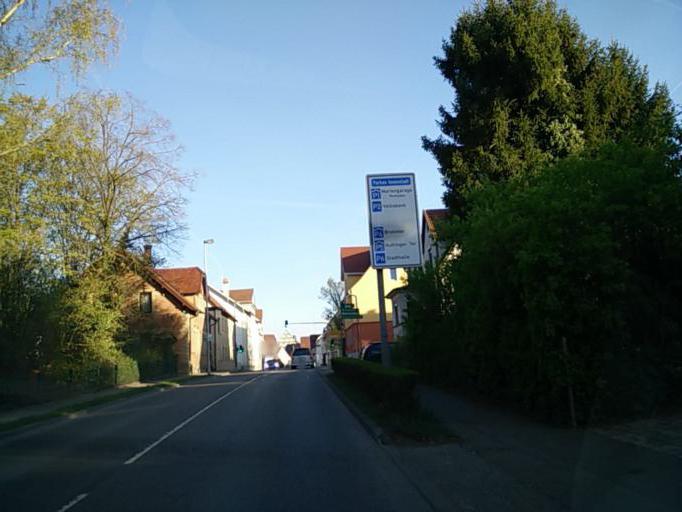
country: DE
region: Baden-Wuerttemberg
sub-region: Regierungsbezirk Stuttgart
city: Herrenberg
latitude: 48.5936
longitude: 8.8746
